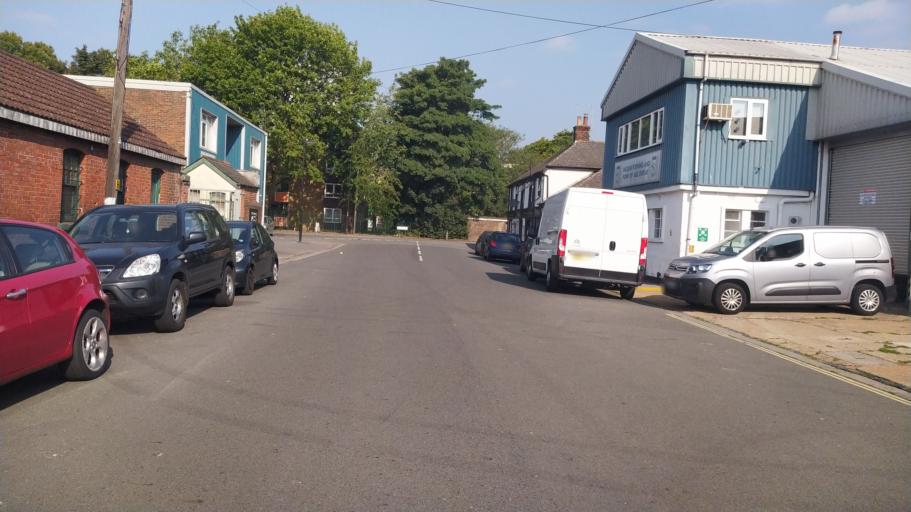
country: GB
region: England
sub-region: Southampton
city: Southampton
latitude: 50.9101
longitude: -1.3844
